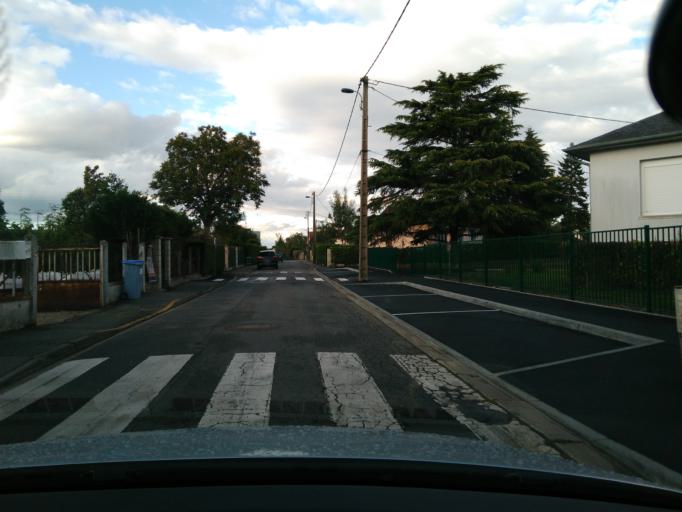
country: FR
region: Haute-Normandie
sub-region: Departement de l'Eure
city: Evreux
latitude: 49.0195
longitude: 1.1650
